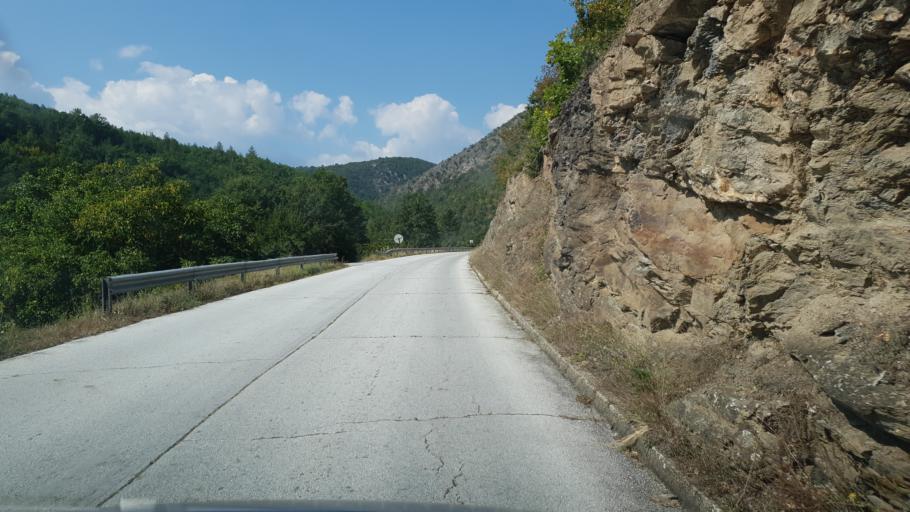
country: MK
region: Makedonski Brod
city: Samokov
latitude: 41.6685
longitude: 21.2467
